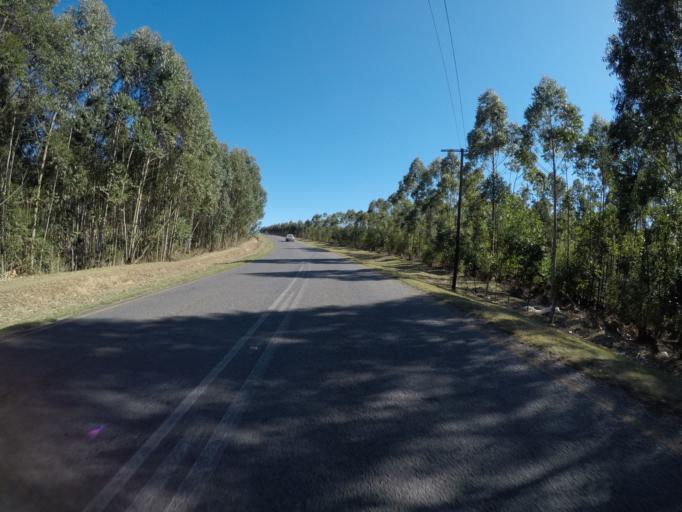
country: ZA
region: Eastern Cape
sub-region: OR Tambo District Municipality
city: Mthatha
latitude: -31.7756
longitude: 28.7377
